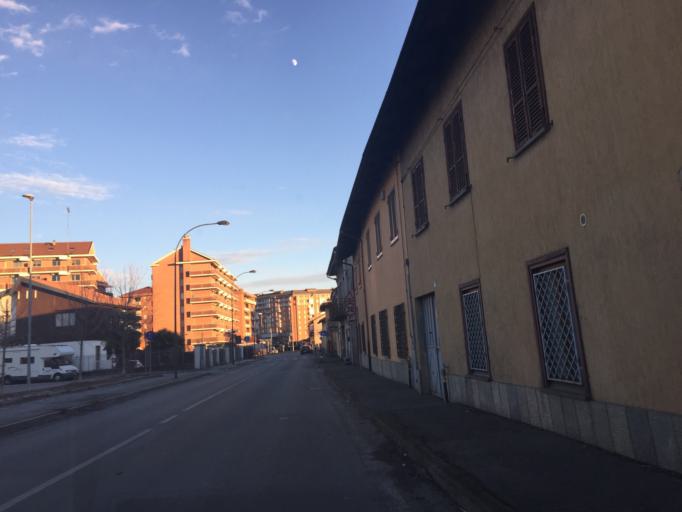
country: IT
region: Piedmont
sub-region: Provincia di Torino
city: Gerbido
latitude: 45.0453
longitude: 7.6143
